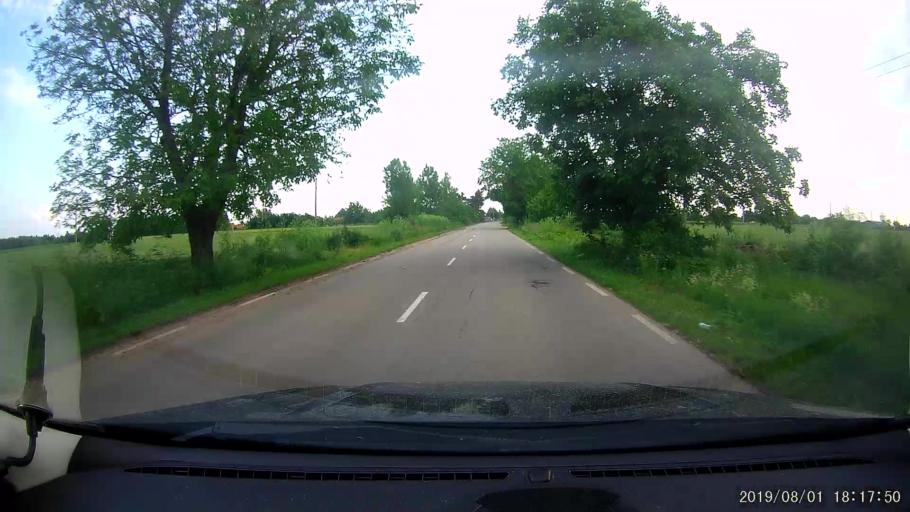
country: BG
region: Shumen
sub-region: Obshtina Kaolinovo
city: Kaolinovo
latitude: 43.7056
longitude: 27.0813
